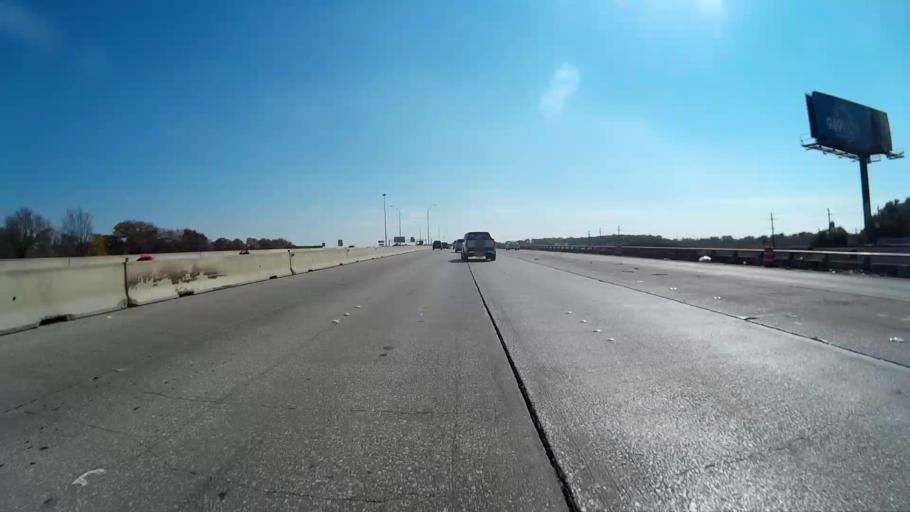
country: US
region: Texas
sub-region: Dallas County
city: Dallas
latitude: 32.7541
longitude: -96.7714
